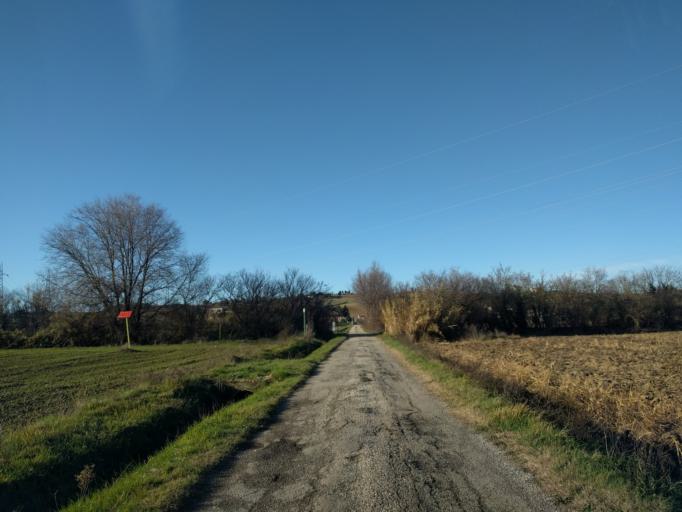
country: IT
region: The Marches
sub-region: Provincia di Pesaro e Urbino
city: Cuccurano
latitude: 43.7842
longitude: 12.9514
